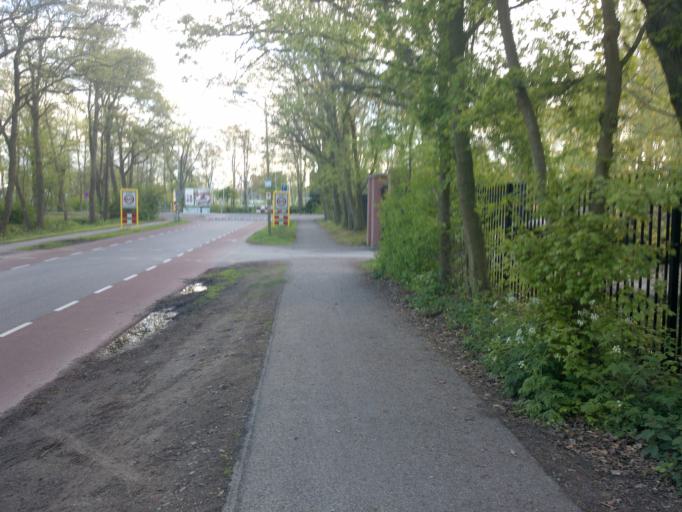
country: NL
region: South Holland
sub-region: Gemeente Lisse
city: Lisse
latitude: 52.2600
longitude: 4.5401
